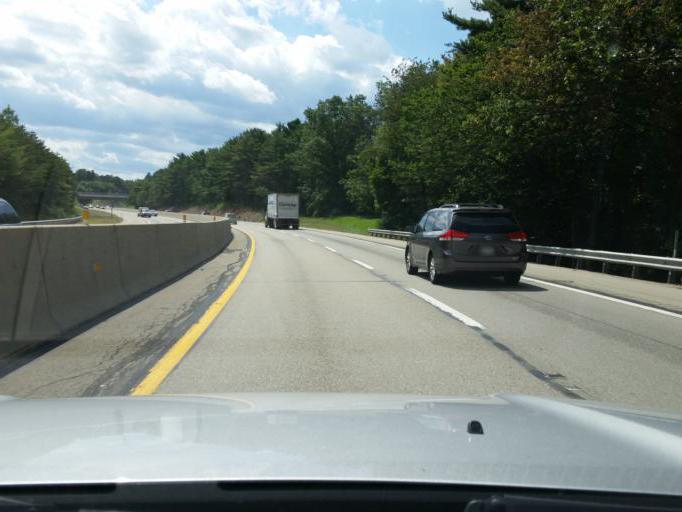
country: US
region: Pennsylvania
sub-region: Fulton County
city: McConnellsburg
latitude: 40.0450
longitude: -78.0228
